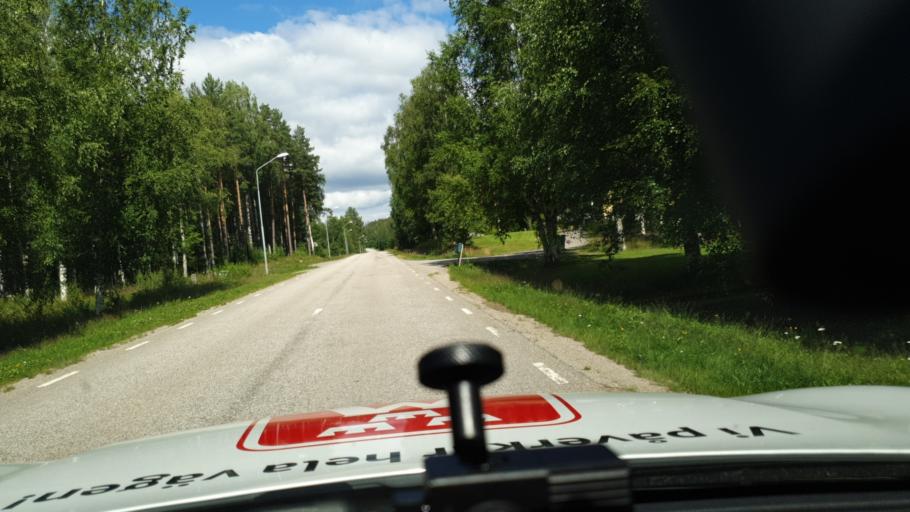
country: NO
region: Hedmark
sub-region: Trysil
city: Innbygda
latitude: 60.9621
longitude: 12.4765
